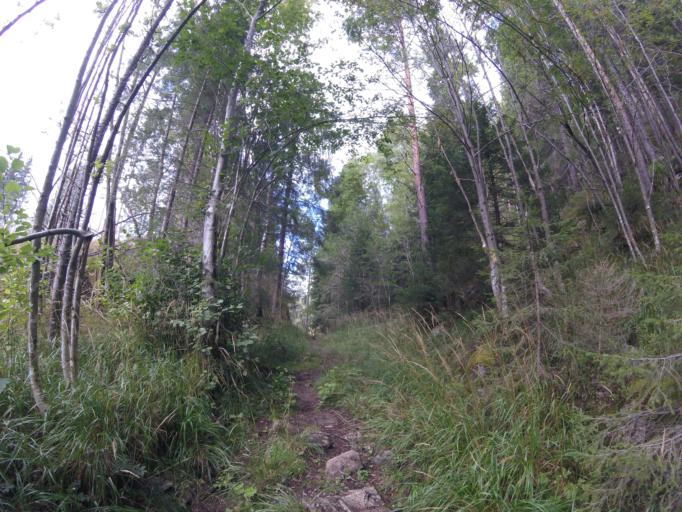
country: NO
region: Akershus
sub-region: Raelingen
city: Fjerdingby
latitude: 59.9195
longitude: 11.0320
